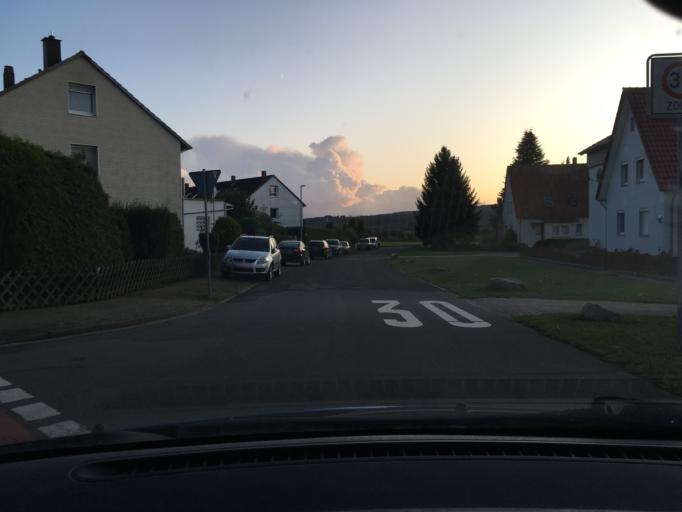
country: DE
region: Lower Saxony
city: Bad Munder am Deister
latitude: 52.2054
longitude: 9.4616
